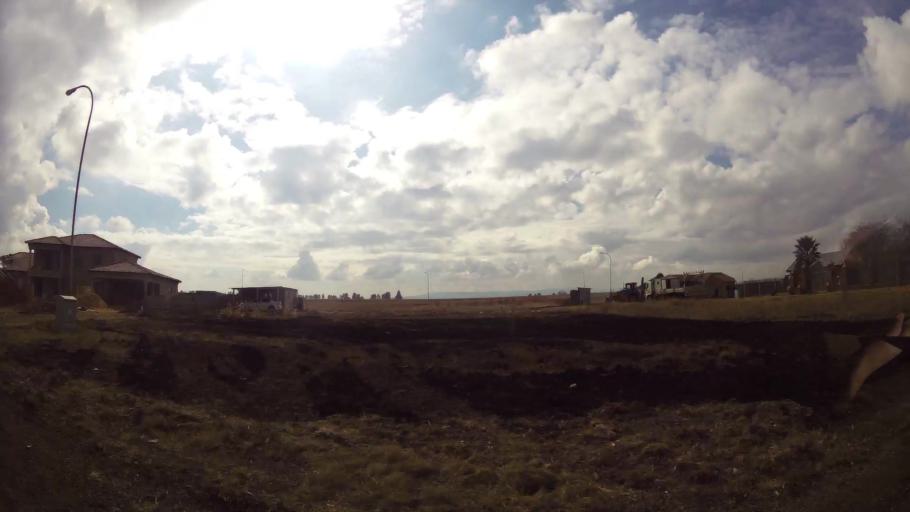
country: ZA
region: Gauteng
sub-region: Sedibeng District Municipality
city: Meyerton
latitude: -26.6018
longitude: 28.0496
